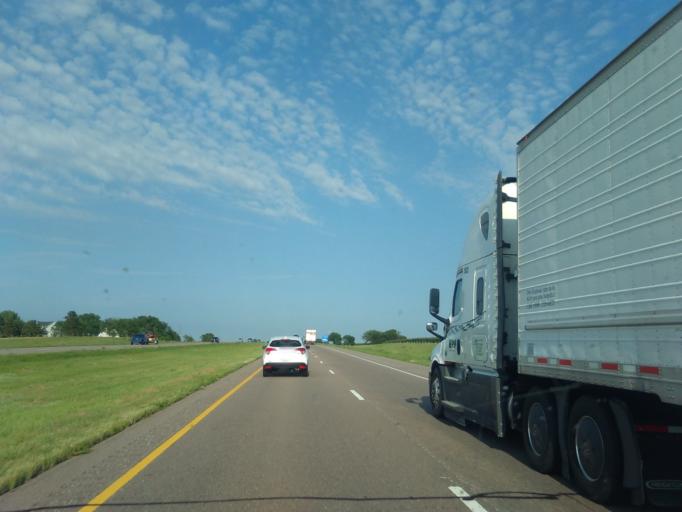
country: US
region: Nebraska
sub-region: York County
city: York
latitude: 40.8212
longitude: -97.6688
